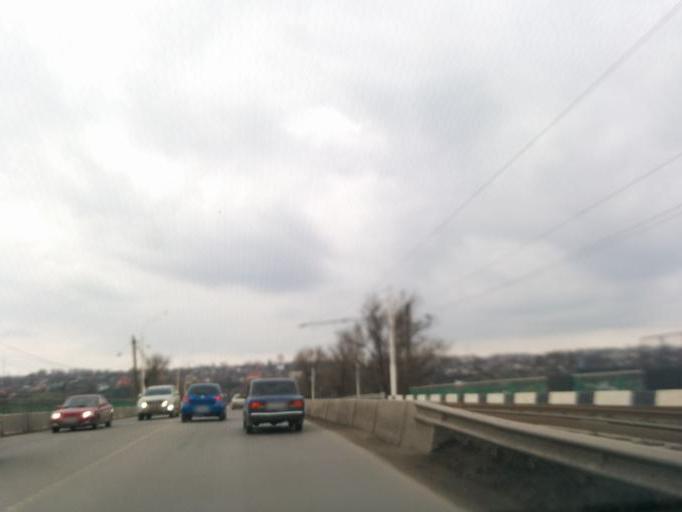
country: RU
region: Rostov
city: Novocherkassk
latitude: 47.4358
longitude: 40.0994
